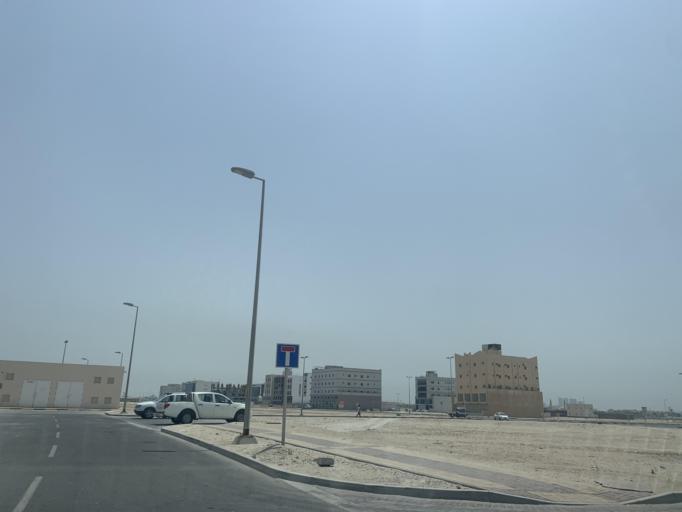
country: BH
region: Muharraq
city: Al Hadd
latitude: 26.2606
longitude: 50.6675
